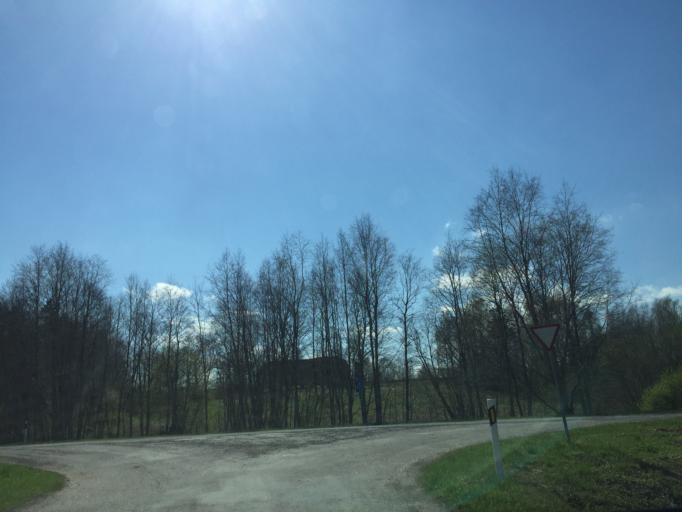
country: EE
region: Tartu
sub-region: Puhja vald
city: Puhja
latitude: 58.1533
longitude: 26.2231
